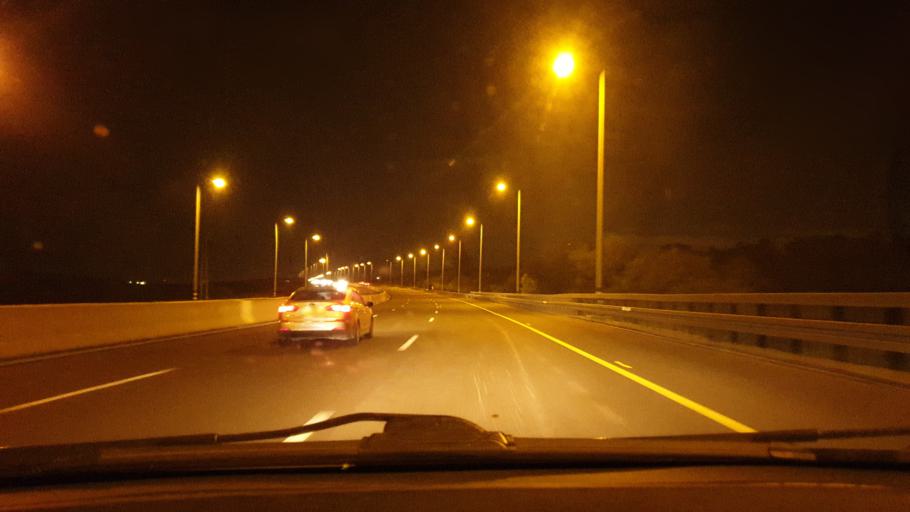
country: IL
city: Nof Ayalon
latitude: 31.8625
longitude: 34.9783
